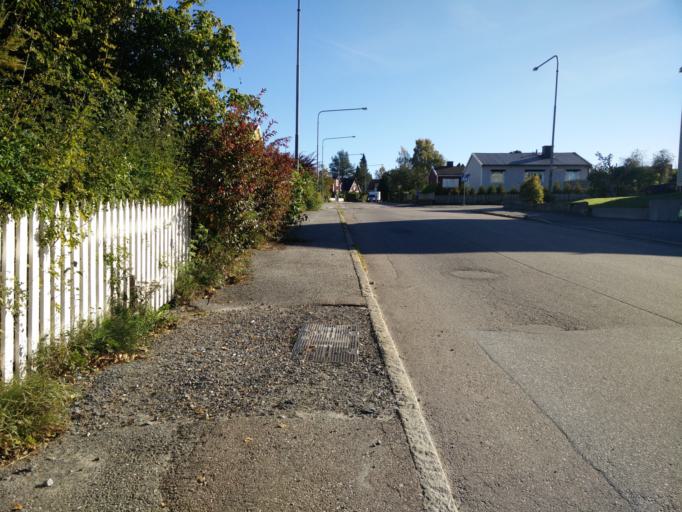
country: SE
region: Vaesternorrland
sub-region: Haernoesands Kommun
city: Haernoesand
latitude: 62.6391
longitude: 17.9580
